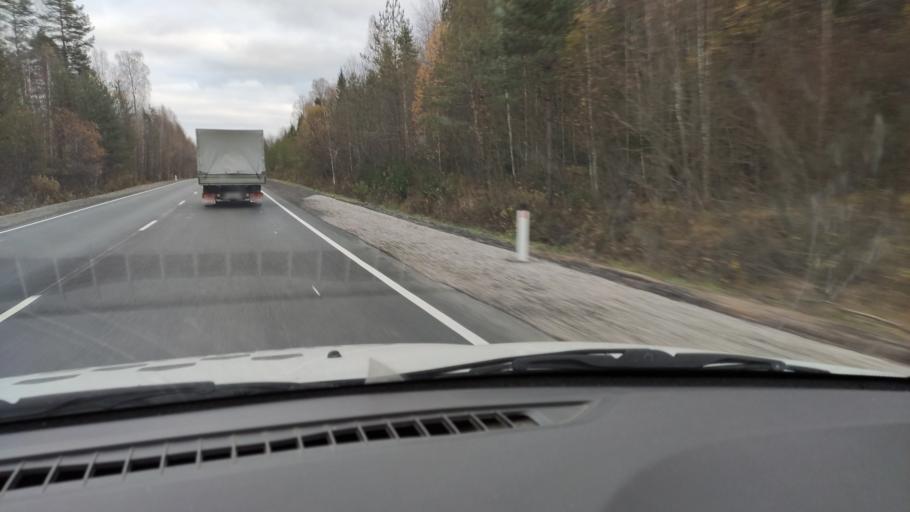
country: RU
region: Kirov
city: Chernaya Kholunitsa
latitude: 58.8721
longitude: 51.5249
